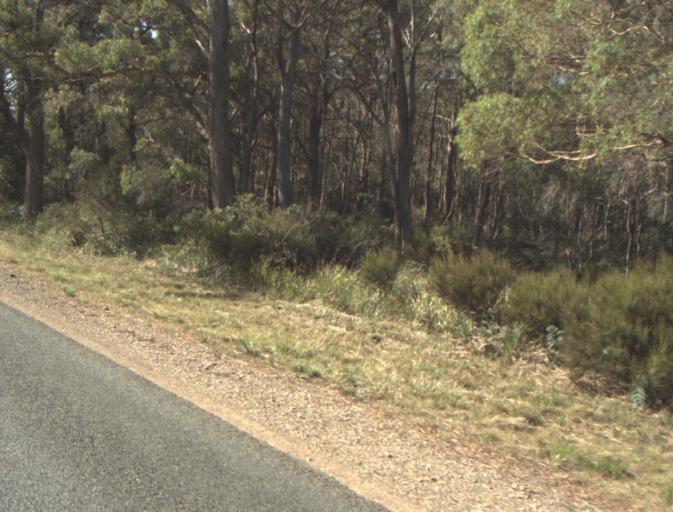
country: AU
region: Tasmania
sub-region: Launceston
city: Mayfield
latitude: -41.3079
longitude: 147.1336
